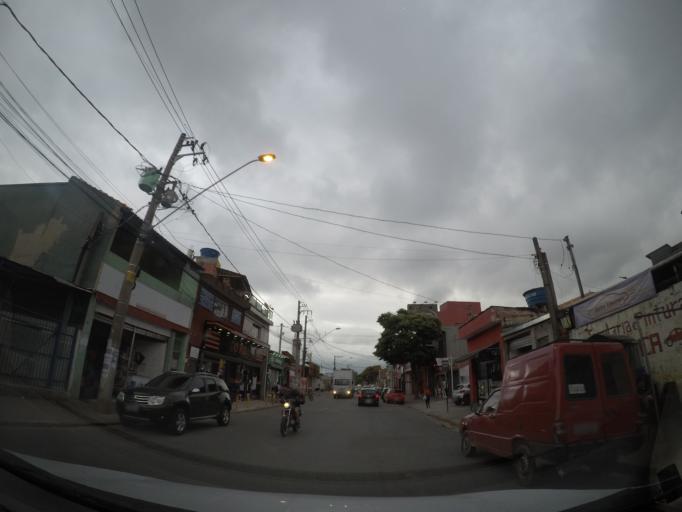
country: BR
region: Sao Paulo
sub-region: Aruja
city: Aruja
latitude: -23.4002
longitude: -46.4311
